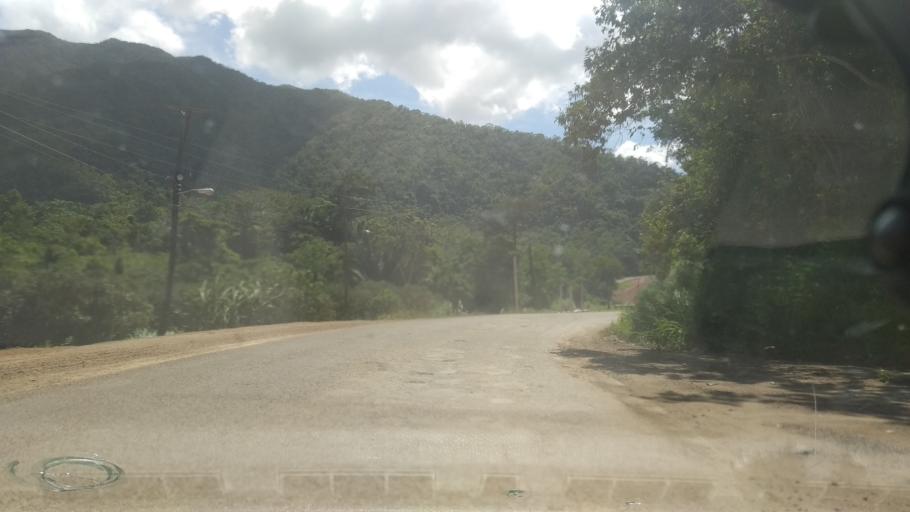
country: BZ
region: Cayo
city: Belmopan
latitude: 17.0559
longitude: -88.5795
